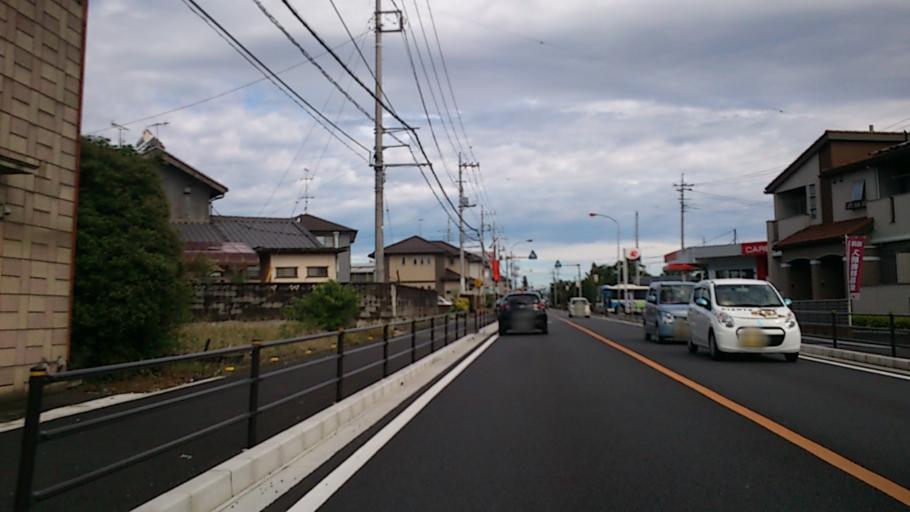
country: JP
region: Saitama
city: Fukayacho
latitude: 36.1979
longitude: 139.2603
